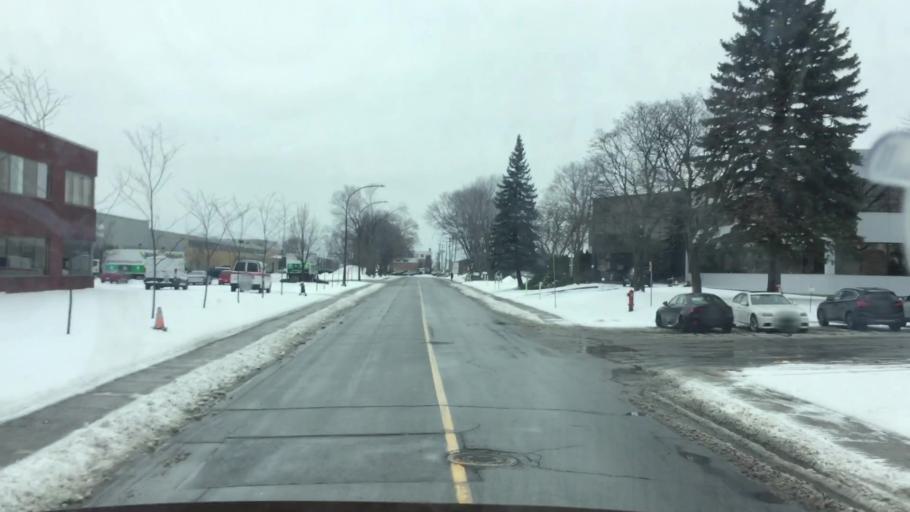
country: CA
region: Quebec
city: Dorval
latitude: 45.4579
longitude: -73.7204
